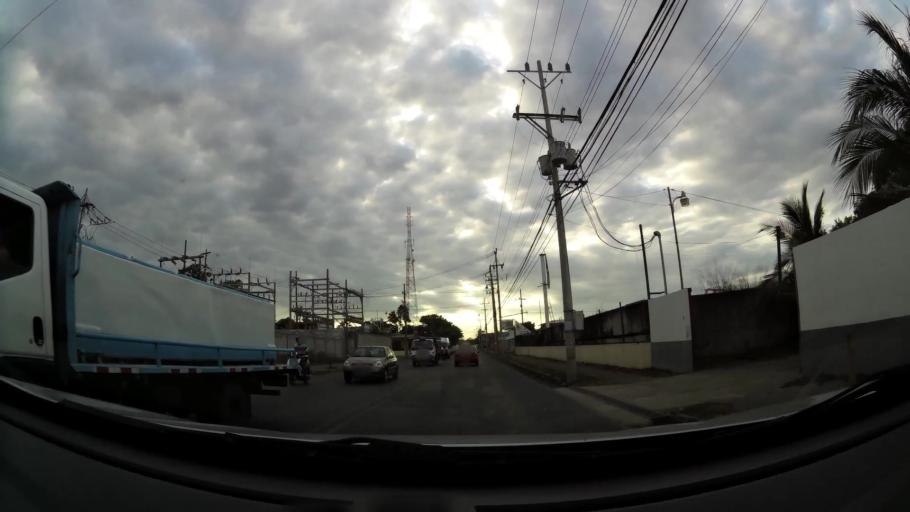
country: CR
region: Puntarenas
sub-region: Canton Central de Puntarenas
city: Puntarenas
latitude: 9.9789
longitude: -84.8220
